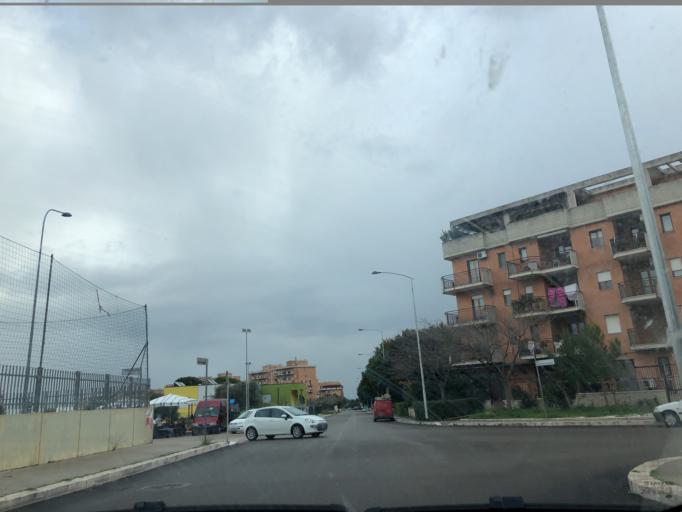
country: IT
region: Apulia
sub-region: Provincia di Foggia
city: Lucera
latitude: 41.5008
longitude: 15.3491
